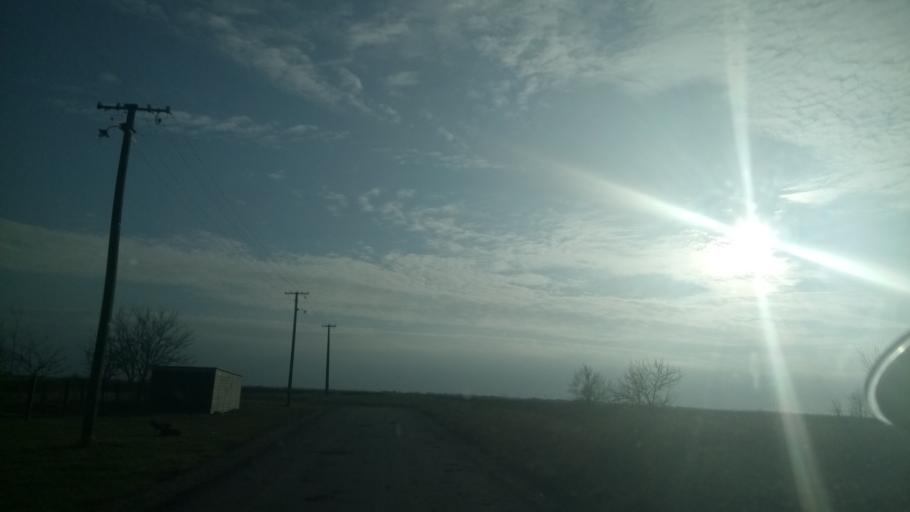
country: RS
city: Vojka
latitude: 44.9363
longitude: 20.1290
